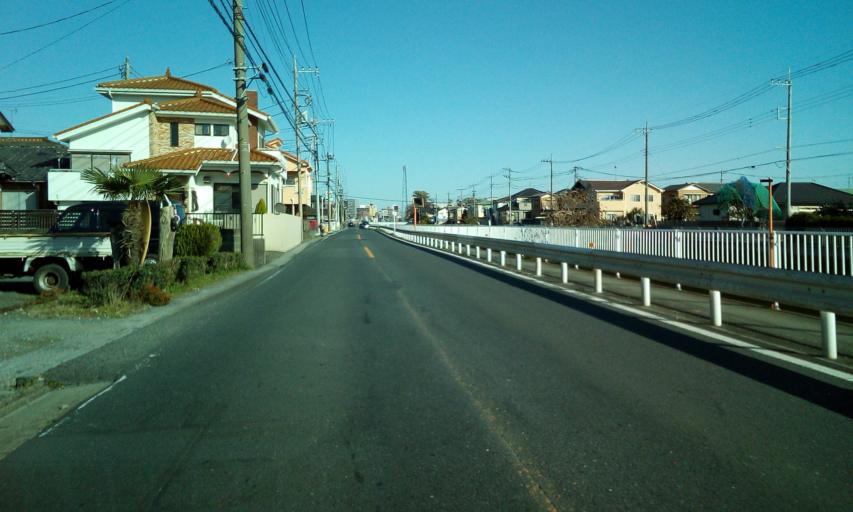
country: JP
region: Chiba
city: Nagareyama
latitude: 35.8316
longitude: 139.8833
